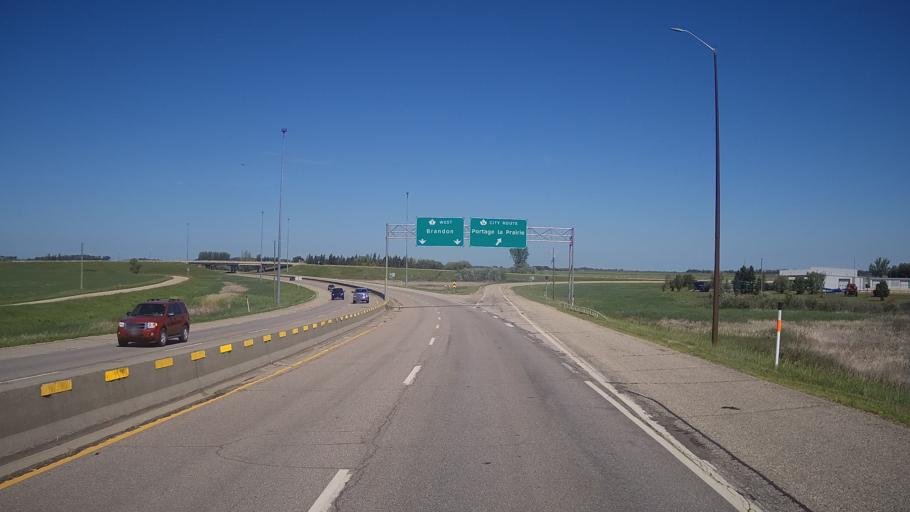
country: CA
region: Manitoba
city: Portage la Prairie
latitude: 49.9701
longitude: -98.3586
